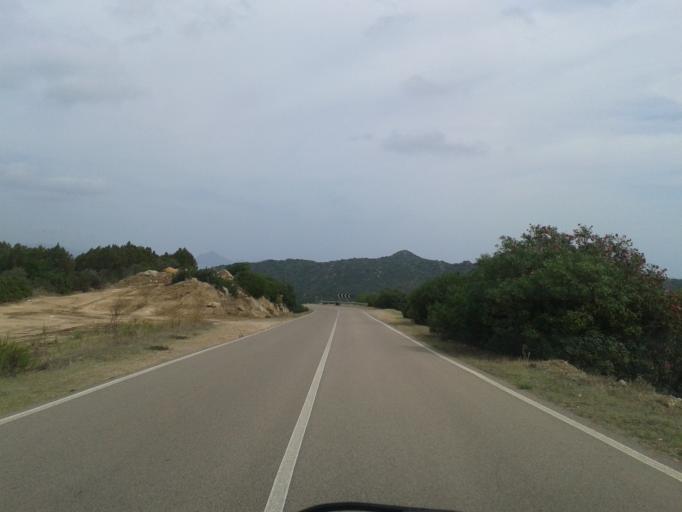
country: IT
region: Sardinia
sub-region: Provincia di Cagliari
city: Villasimius
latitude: 39.1684
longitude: 9.5608
